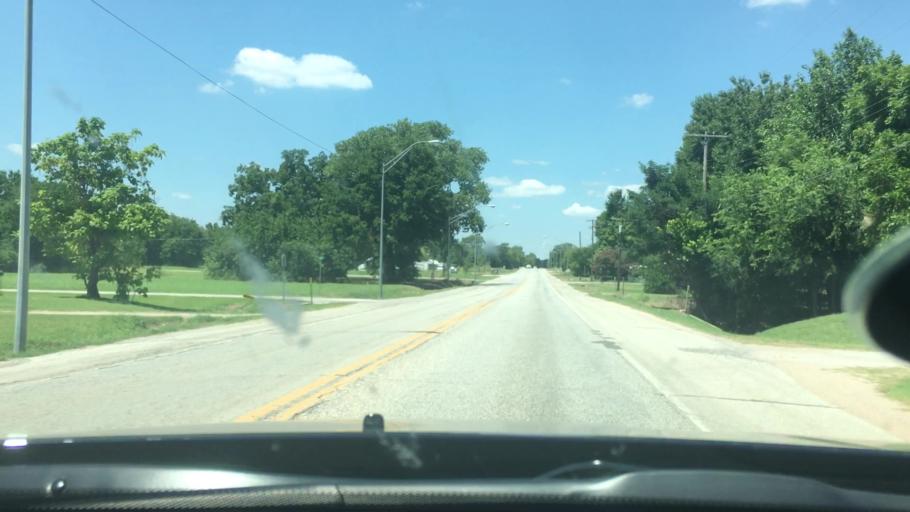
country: US
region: Oklahoma
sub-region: Carter County
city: Dickson
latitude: 34.1863
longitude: -96.8827
